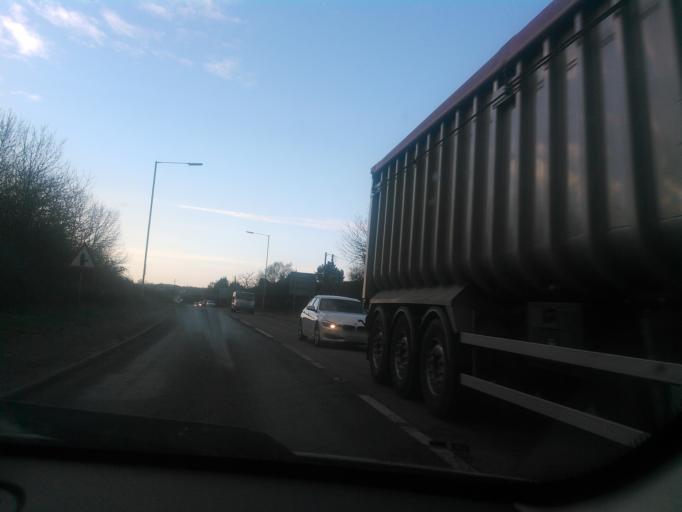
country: GB
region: England
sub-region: Shropshire
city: Stoke upon Tern
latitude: 52.8865
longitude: -2.5434
